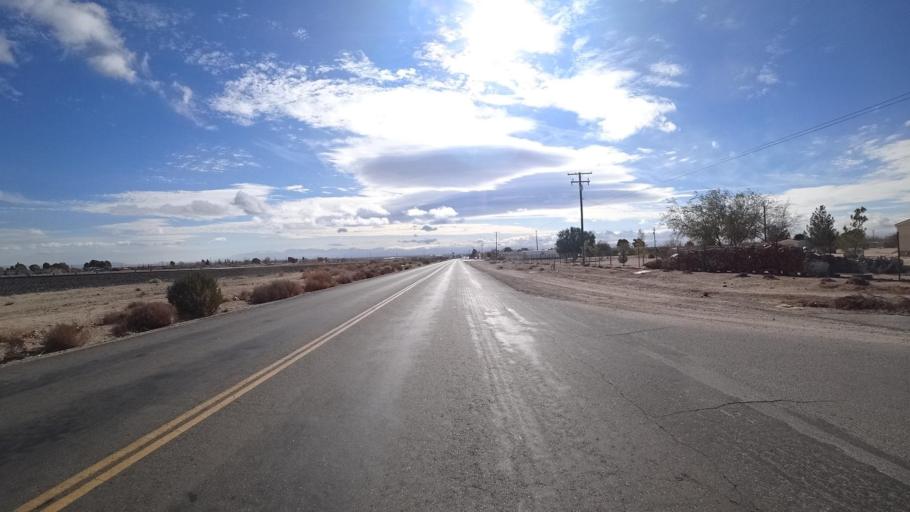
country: US
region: California
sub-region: Kern County
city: Rosamond
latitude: 34.8718
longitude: -118.1642
